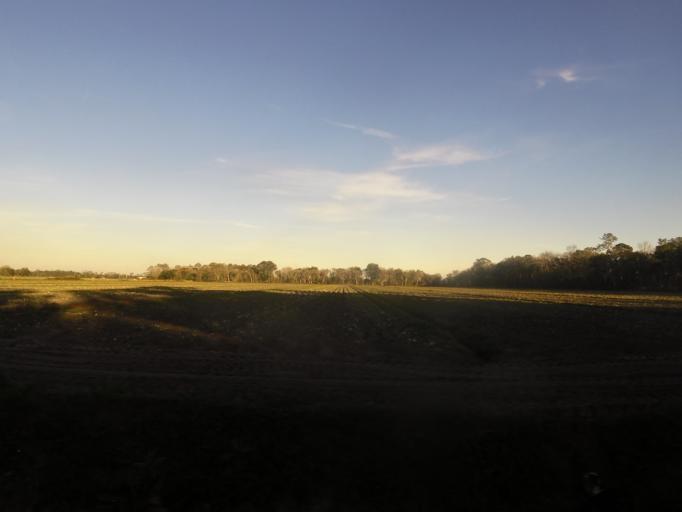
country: US
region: Florida
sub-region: Saint Johns County
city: Saint Augustine Shores
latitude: 29.7883
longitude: -81.4588
